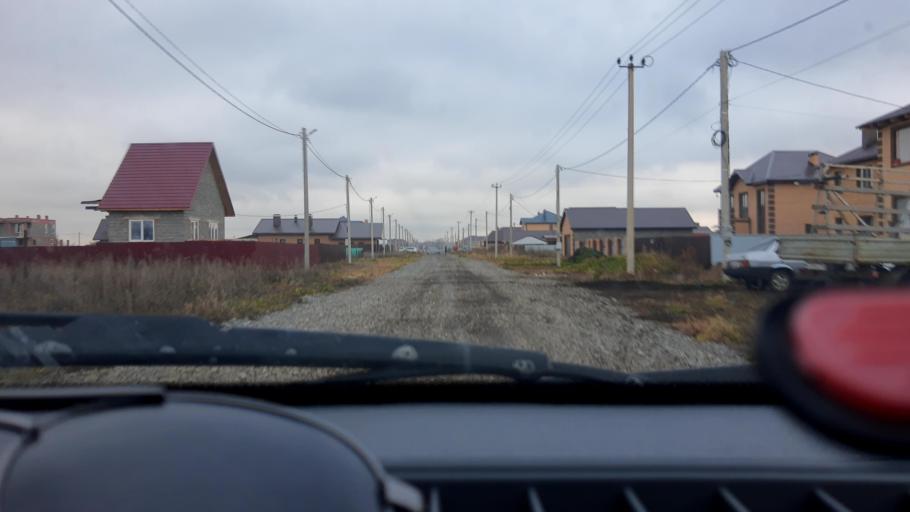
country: RU
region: Bashkortostan
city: Ufa
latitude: 54.6087
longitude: 55.9166
